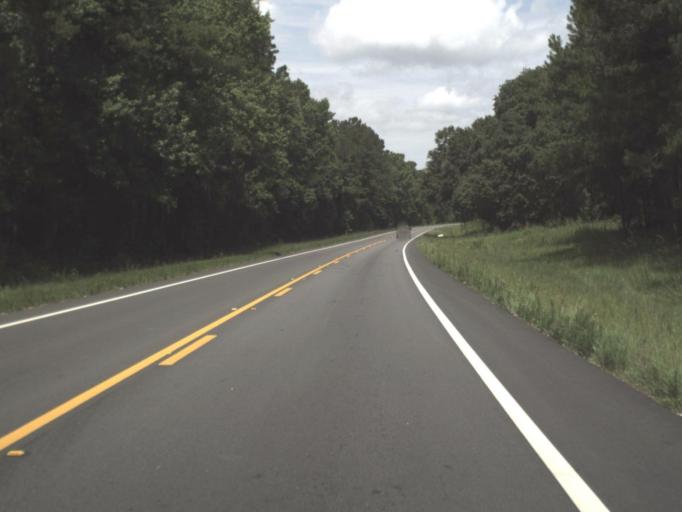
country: US
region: Florida
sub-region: Jefferson County
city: Monticello
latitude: 30.4729
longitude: -83.6616
